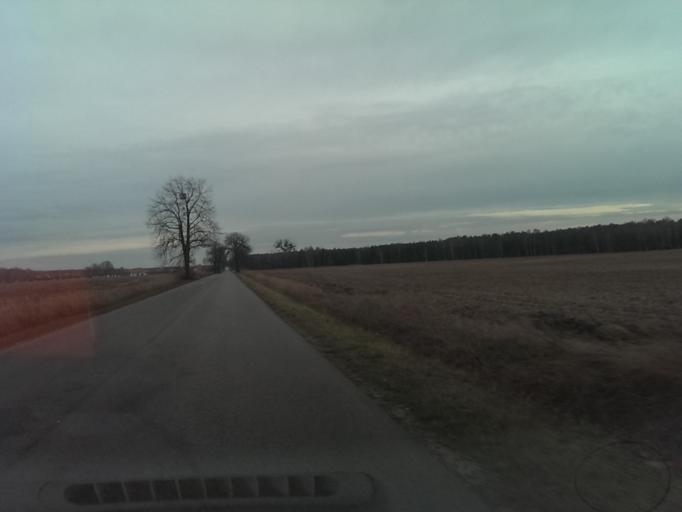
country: PL
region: Kujawsko-Pomorskie
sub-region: Powiat nakielski
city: Szubin
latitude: 53.0822
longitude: 17.7781
